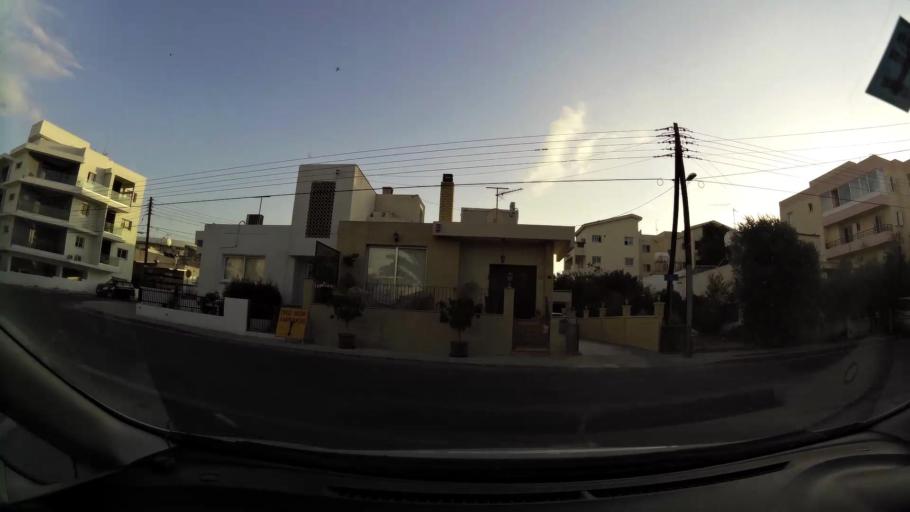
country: CY
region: Lefkosia
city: Nicosia
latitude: 35.1563
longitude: 33.4010
